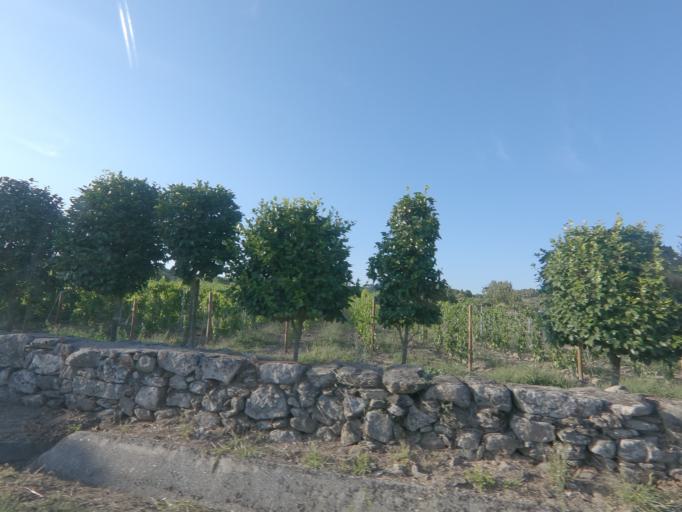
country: PT
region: Vila Real
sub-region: Sabrosa
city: Sabrosa
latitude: 41.2747
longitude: -7.5110
